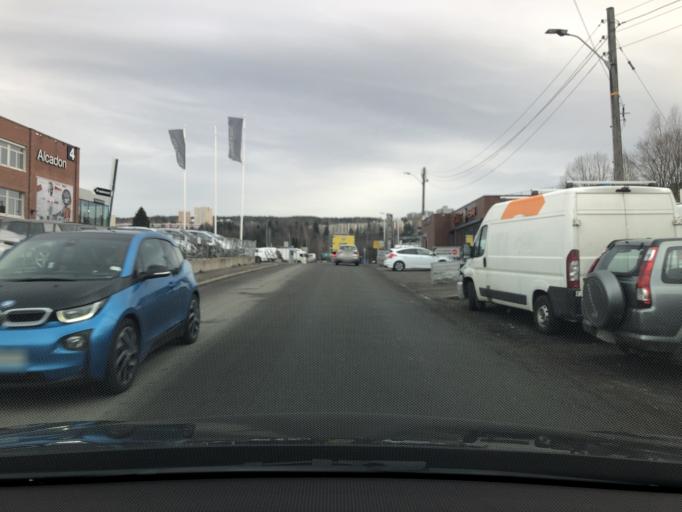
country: NO
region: Oslo
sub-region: Oslo
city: Oslo
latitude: 59.9294
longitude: 10.8457
